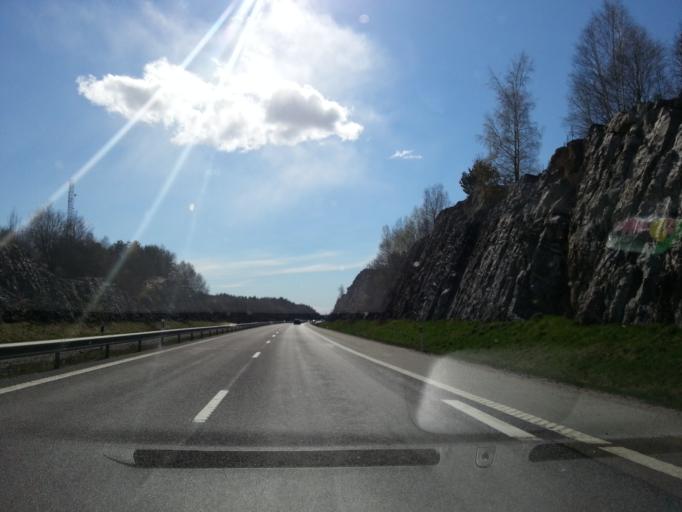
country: SE
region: Vaestra Goetaland
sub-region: Stenungsunds Kommun
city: Stora Hoga
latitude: 58.0533
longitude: 11.8716
